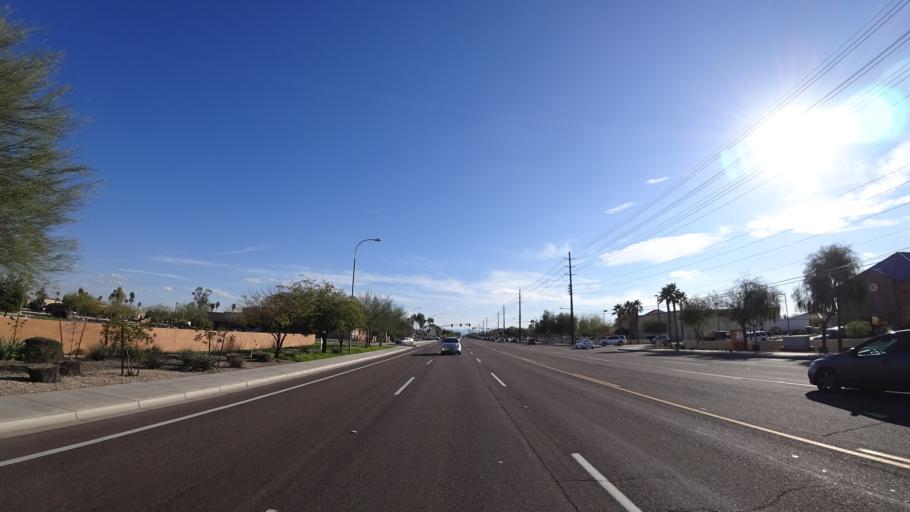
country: US
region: Arizona
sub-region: Maricopa County
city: Peoria
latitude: 33.6114
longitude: -112.2375
